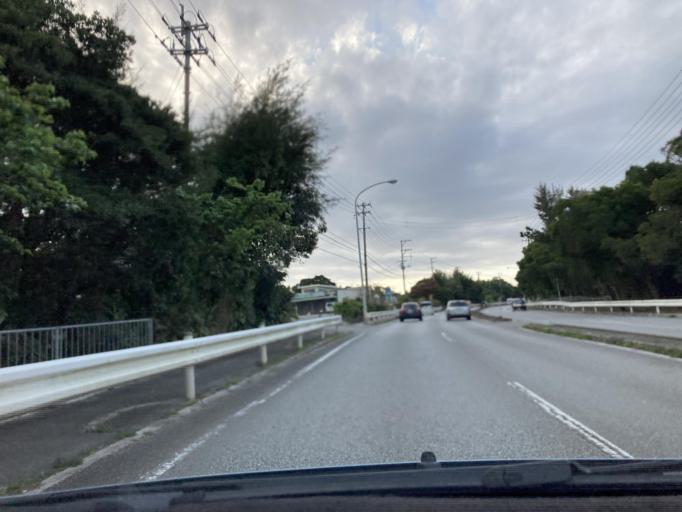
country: JP
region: Okinawa
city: Ishikawa
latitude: 26.4336
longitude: 127.8144
